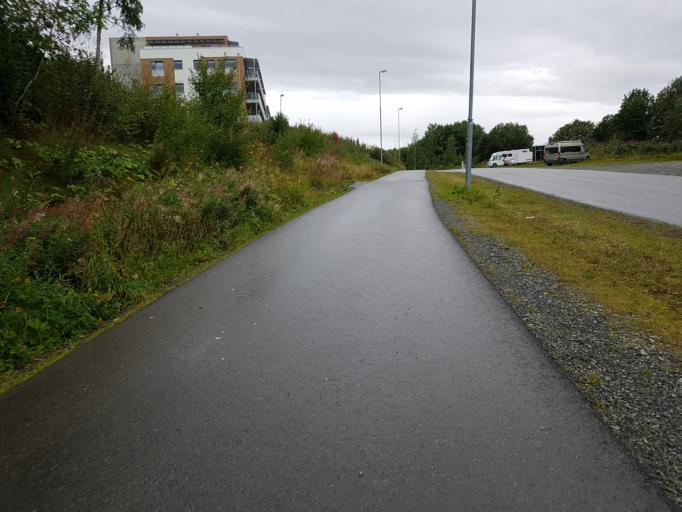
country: NO
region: Sor-Trondelag
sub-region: Trondheim
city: Trondheim
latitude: 63.4095
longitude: 10.4807
